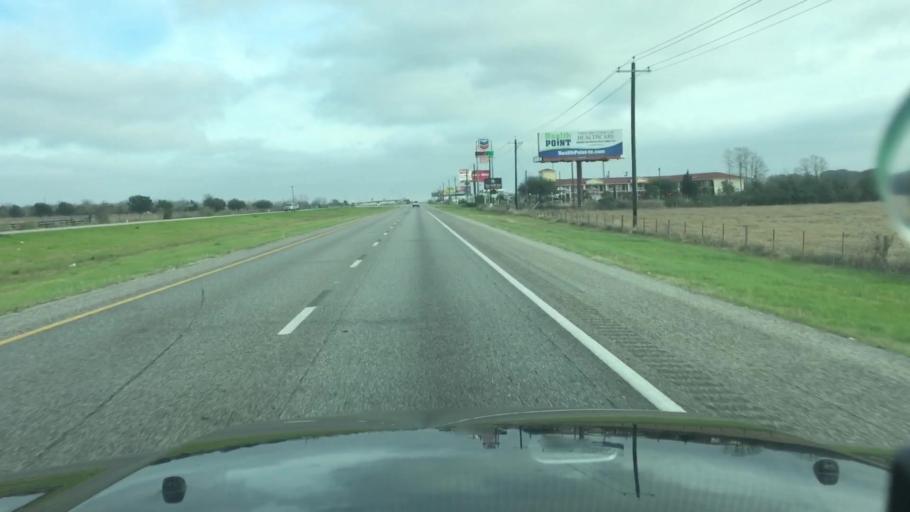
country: US
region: Texas
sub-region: Waller County
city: Hempstead
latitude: 30.1186
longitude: -96.0941
